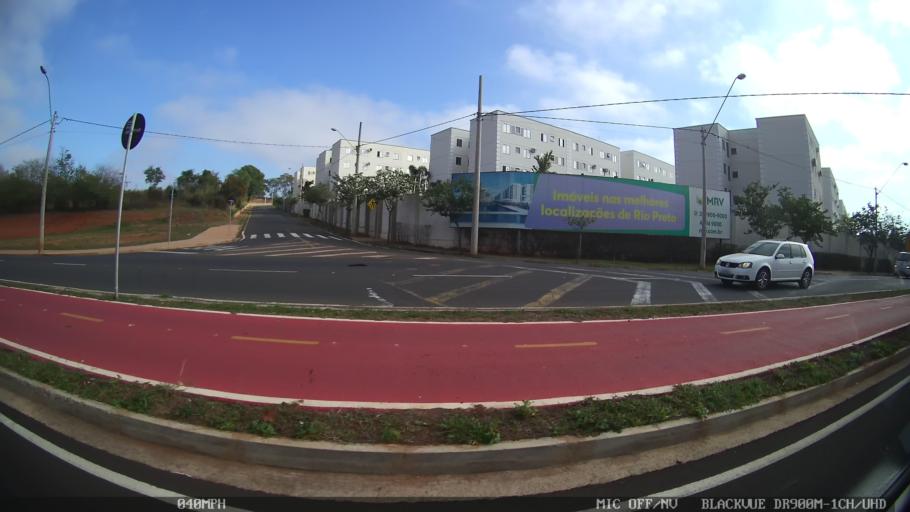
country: BR
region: Sao Paulo
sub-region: Sao Jose Do Rio Preto
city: Sao Jose do Rio Preto
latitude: -20.8079
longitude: -49.4292
